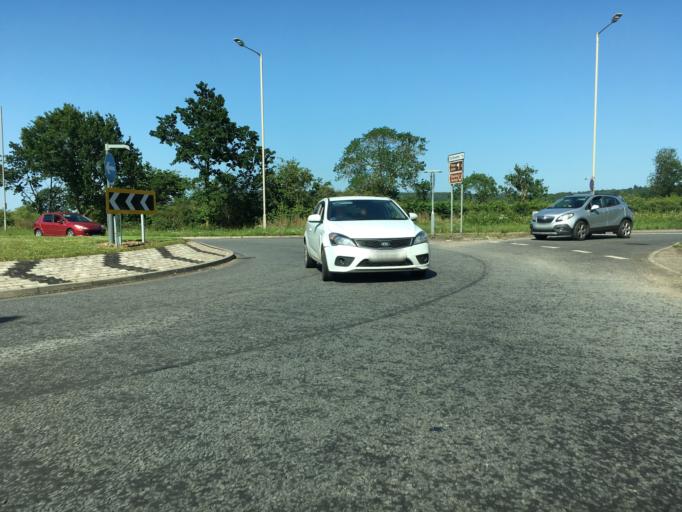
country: GB
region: England
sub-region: Milton Keynes
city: Water Eaton
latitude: 51.9840
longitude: -0.7022
